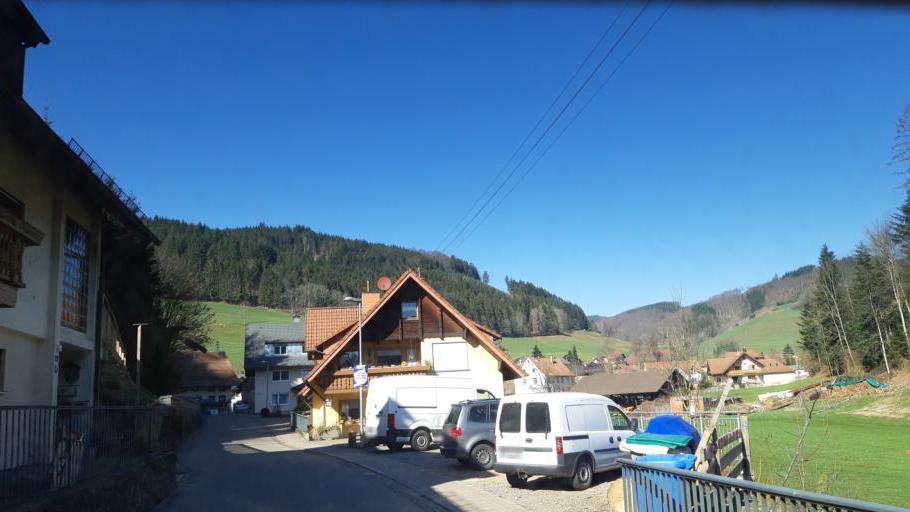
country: DE
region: Baden-Wuerttemberg
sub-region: Freiburg Region
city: Gutach im Breisgau
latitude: 48.1446
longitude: 7.9780
